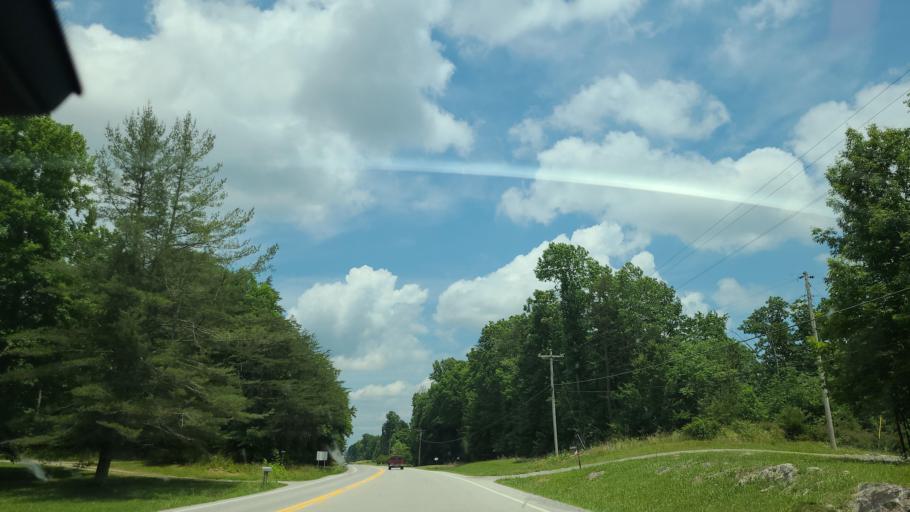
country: US
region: Tennessee
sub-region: Cumberland County
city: Lake Tansi
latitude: 35.7811
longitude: -85.0324
